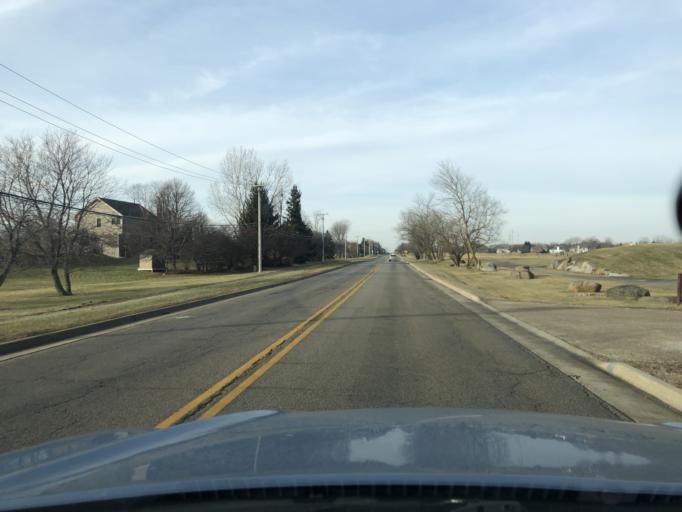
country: US
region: Illinois
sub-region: McHenry County
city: Algonquin
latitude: 42.1540
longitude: -88.3182
